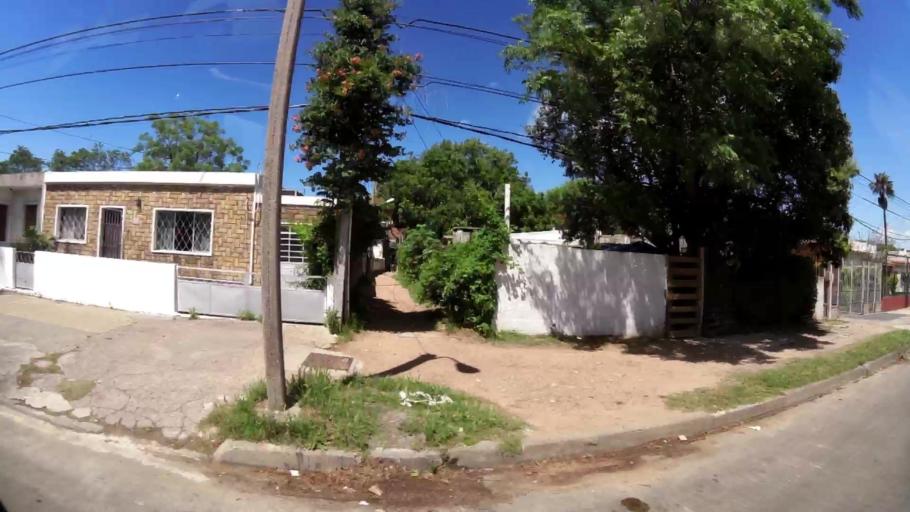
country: UY
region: Montevideo
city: Montevideo
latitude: -34.8588
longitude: -56.1388
